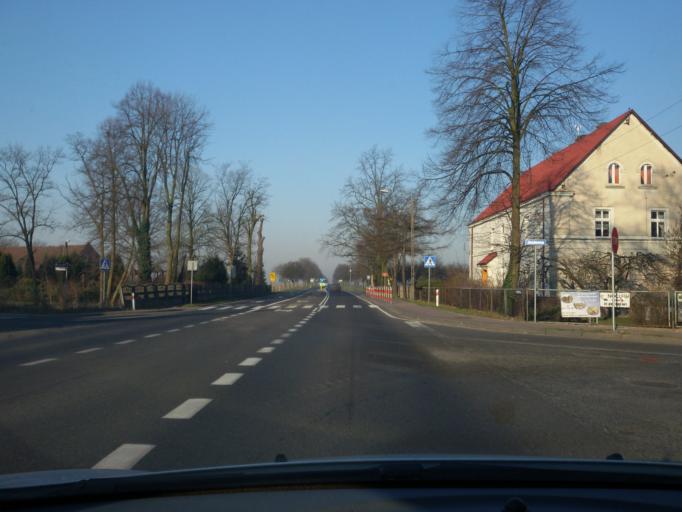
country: PL
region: Greater Poland Voivodeship
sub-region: Powiat leszczynski
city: Swieciechowa
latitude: 51.8247
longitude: 16.4430
